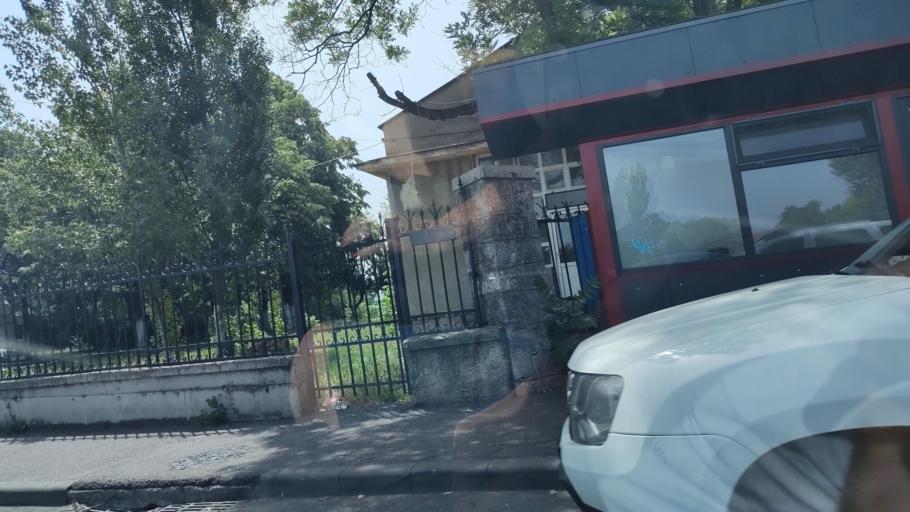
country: RO
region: Mehedinti
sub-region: Municipiul Drobeta-Turnu Severin
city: Drobeta-Turnu Severin
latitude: 44.6247
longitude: 22.6599
